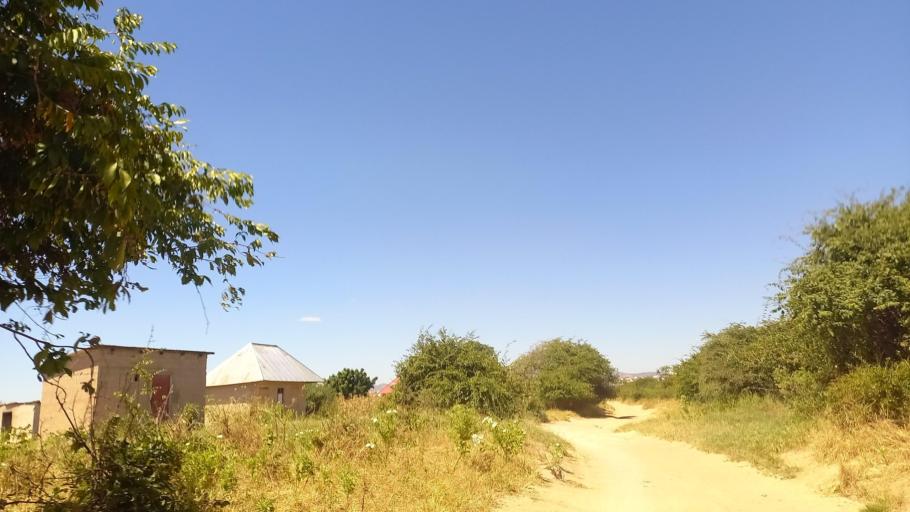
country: TZ
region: Dodoma
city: Dodoma
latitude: -6.1151
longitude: 35.6963
